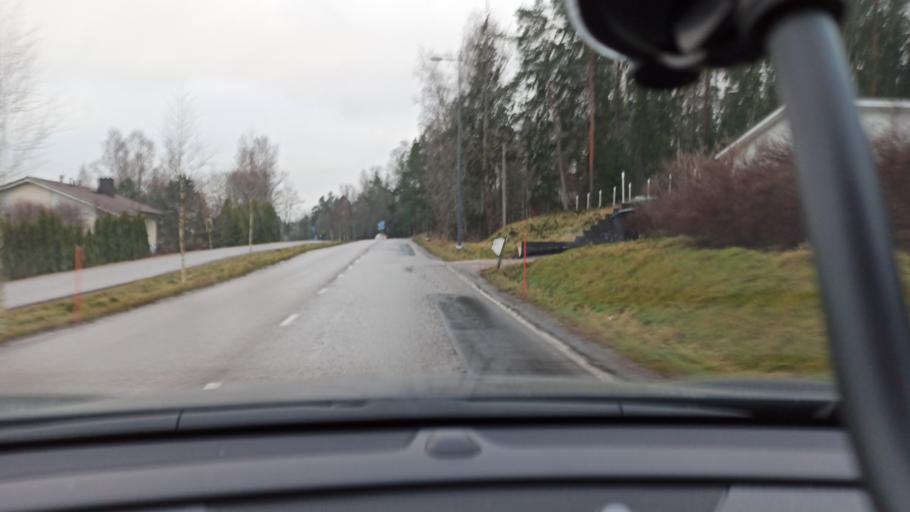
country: FI
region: Uusimaa
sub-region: Helsinki
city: Kirkkonummi
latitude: 60.1237
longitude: 24.4696
